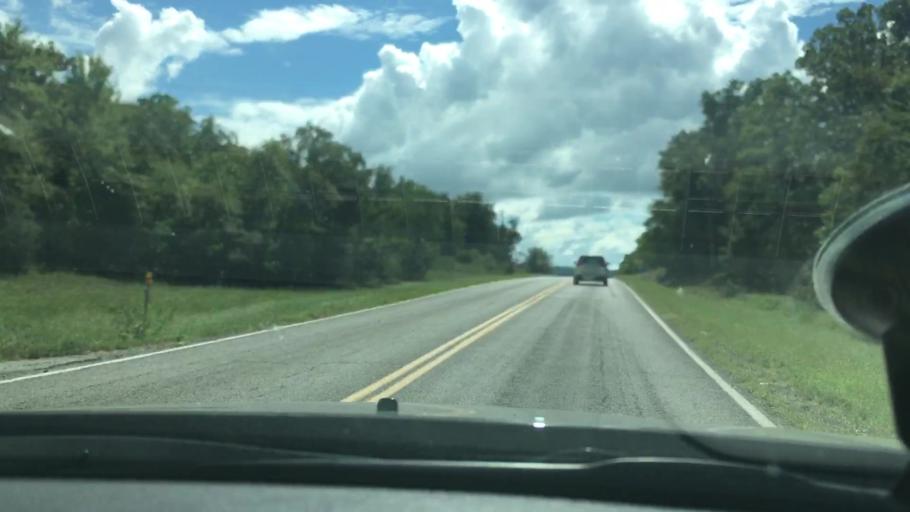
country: US
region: Oklahoma
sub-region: Cherokee County
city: Park Hill
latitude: 35.6869
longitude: -94.9113
